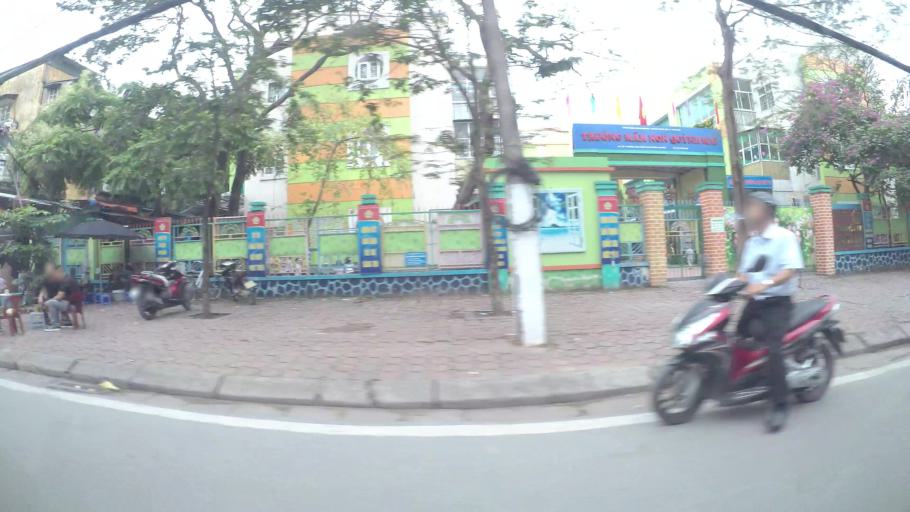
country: VN
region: Ha Noi
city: Hai BaTrung
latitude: 21.0007
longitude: 105.8615
